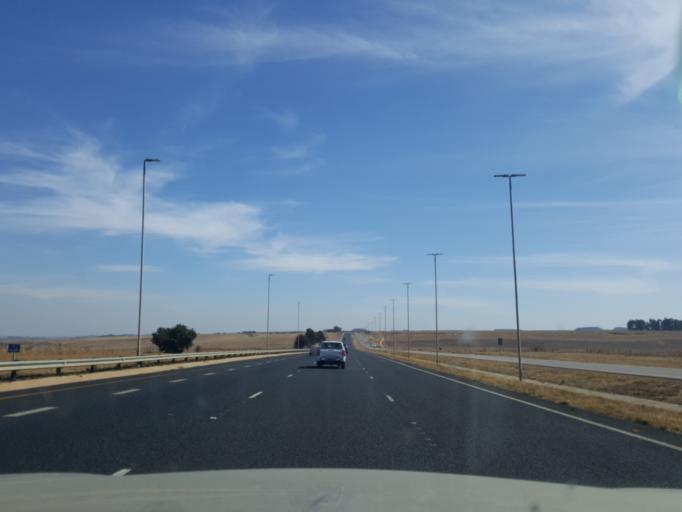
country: ZA
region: Mpumalanga
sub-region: Nkangala District Municipality
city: Belfast
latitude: -25.8320
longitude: 29.7888
